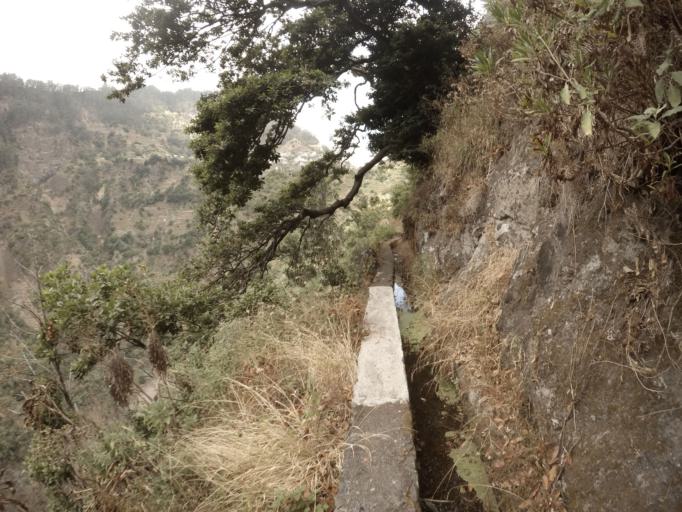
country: PT
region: Madeira
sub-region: Camara de Lobos
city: Curral das Freiras
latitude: 32.6866
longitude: -16.9643
